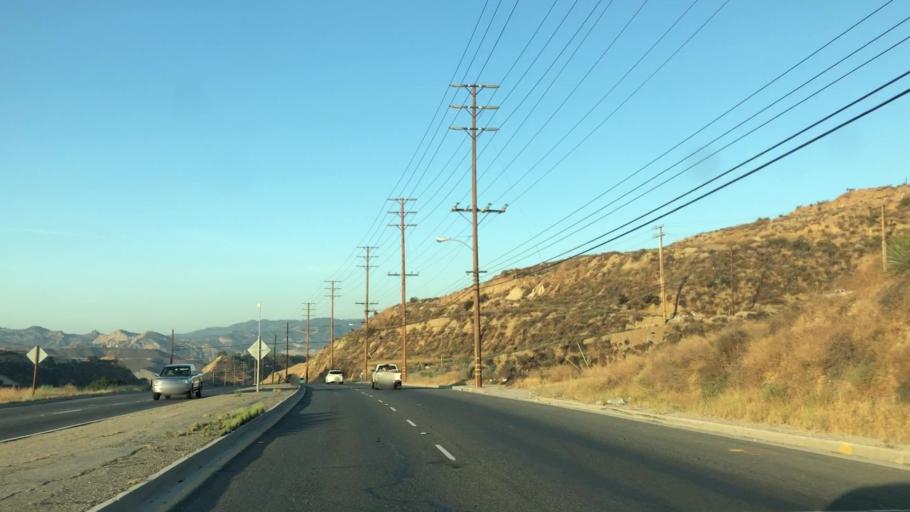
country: US
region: California
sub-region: Los Angeles County
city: Santa Clarita
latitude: 34.3937
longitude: -118.4868
